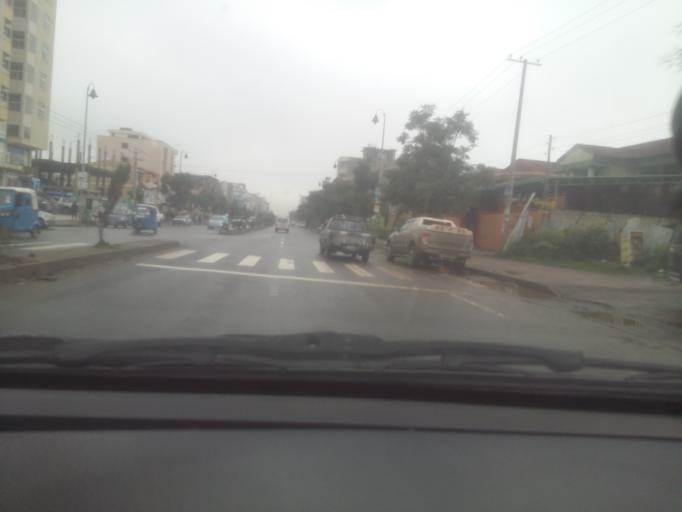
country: ET
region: Adis Abeba
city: Addis Ababa
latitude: 8.9490
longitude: 38.7236
